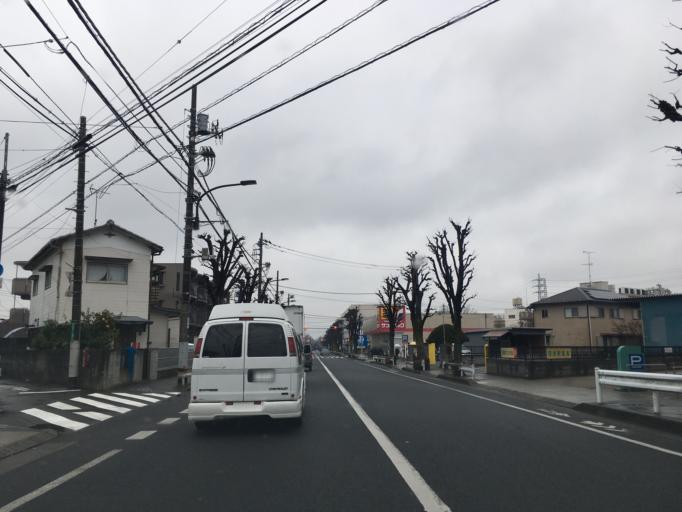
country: JP
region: Tokyo
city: Kokubunji
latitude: 35.7043
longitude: 139.4566
